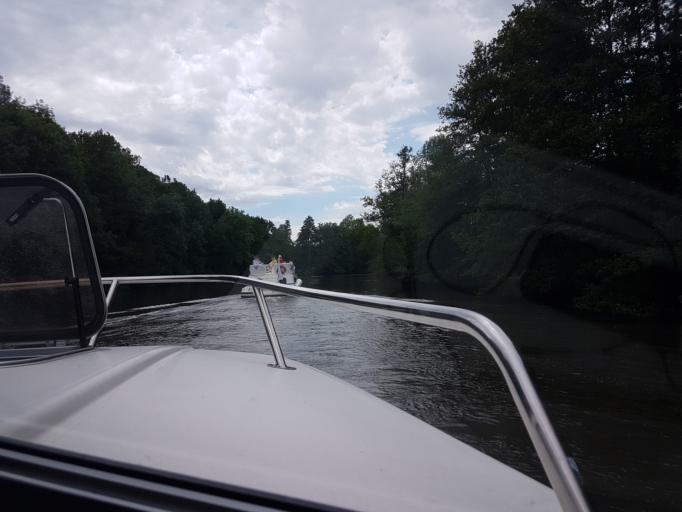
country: FR
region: Bourgogne
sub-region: Departement de la Nievre
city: Clamecy
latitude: 47.4667
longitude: 3.5281
